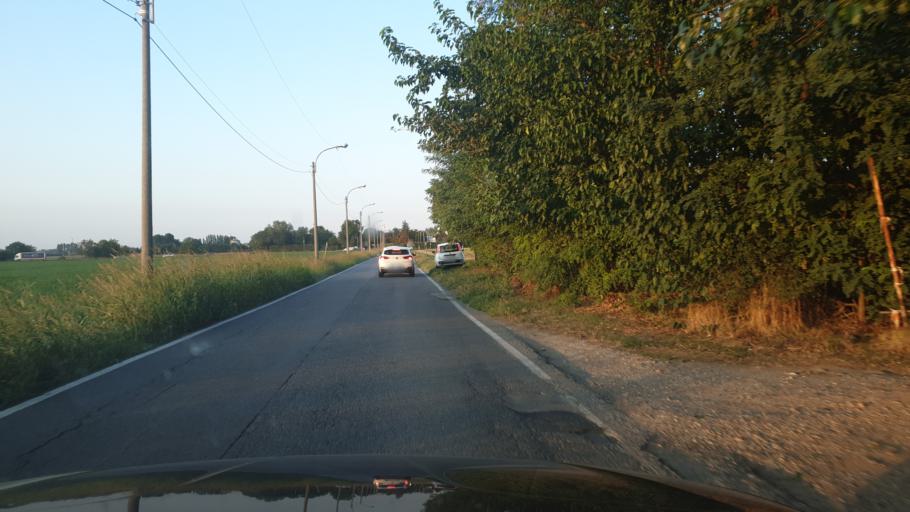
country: IT
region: Emilia-Romagna
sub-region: Provincia di Bologna
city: Quarto Inferiore
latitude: 44.5268
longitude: 11.3816
